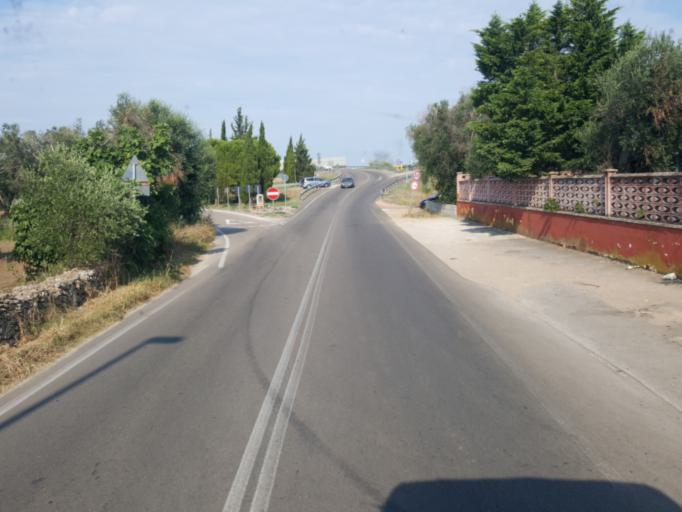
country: IT
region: Apulia
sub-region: Provincia di Lecce
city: Trepuzzi
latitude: 40.4392
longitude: 18.0754
